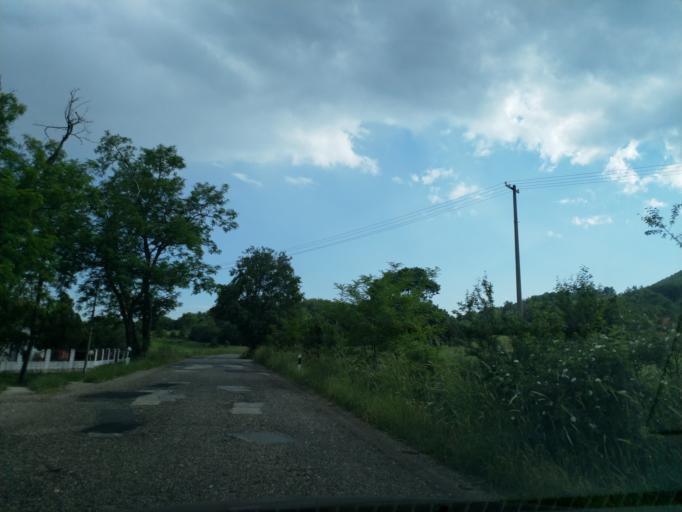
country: RS
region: Central Serbia
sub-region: Zajecarski Okrug
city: Boljevac
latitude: 43.9813
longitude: 21.9732
